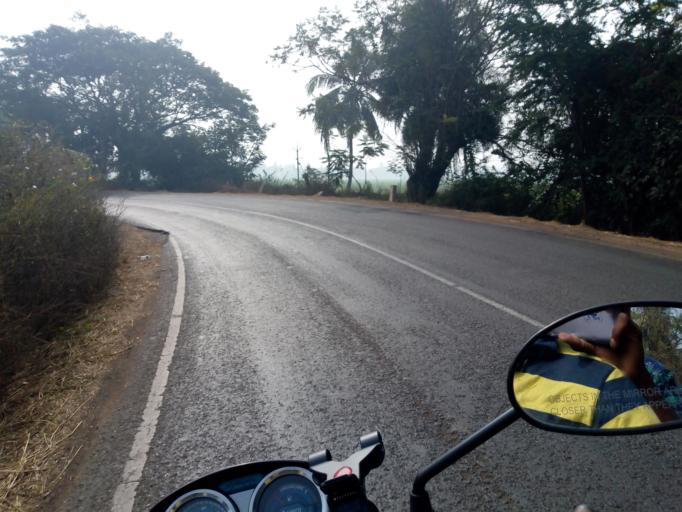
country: IN
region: Andhra Pradesh
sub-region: West Godavari
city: Tadepallegudem
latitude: 16.8008
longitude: 81.4116
